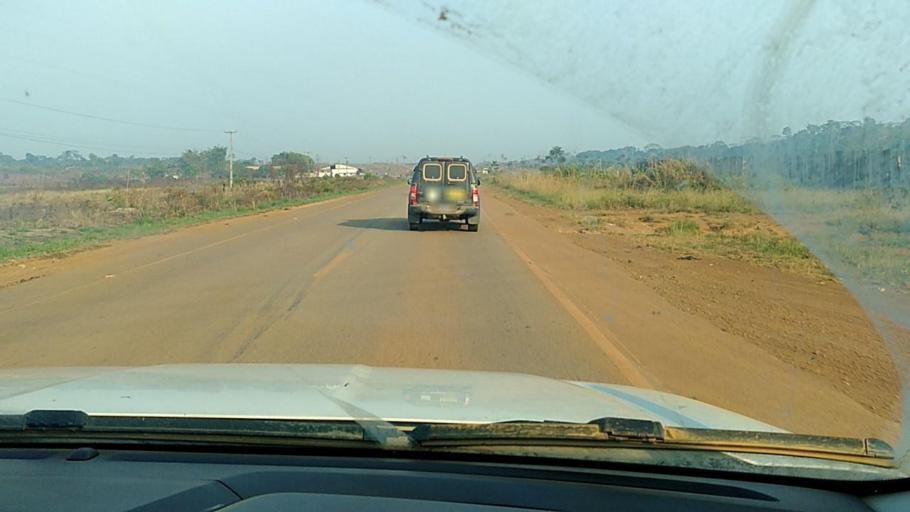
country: BR
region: Rondonia
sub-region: Porto Velho
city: Porto Velho
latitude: -8.7374
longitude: -63.9601
